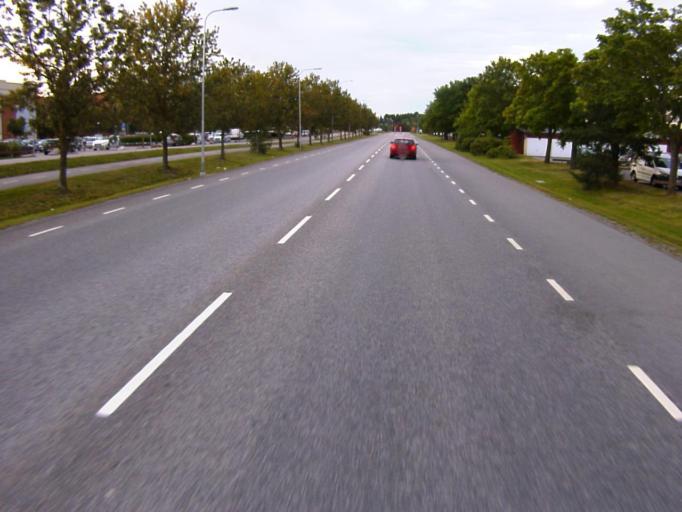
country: SE
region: Soedermanland
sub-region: Eskilstuna Kommun
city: Torshalla
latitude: 59.3942
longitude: 16.4900
